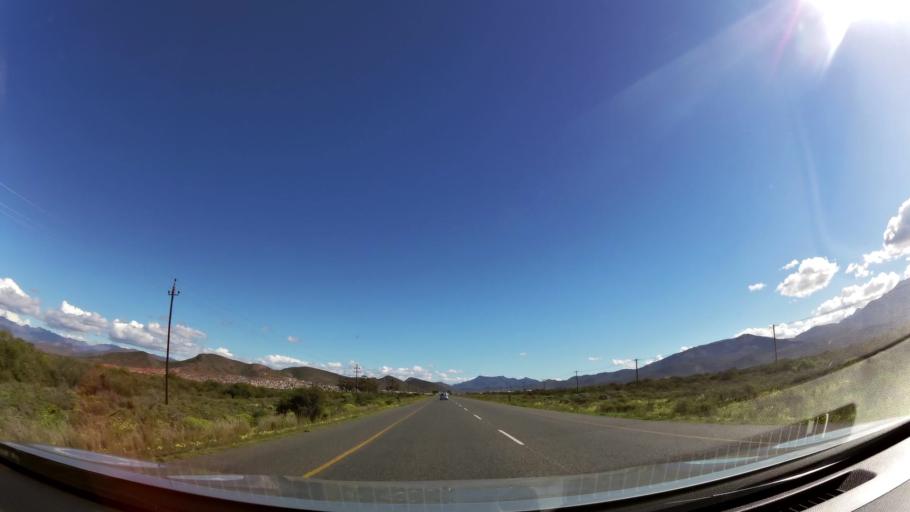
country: ZA
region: Western Cape
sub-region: Cape Winelands District Municipality
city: Ashton
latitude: -33.8145
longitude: 19.9151
